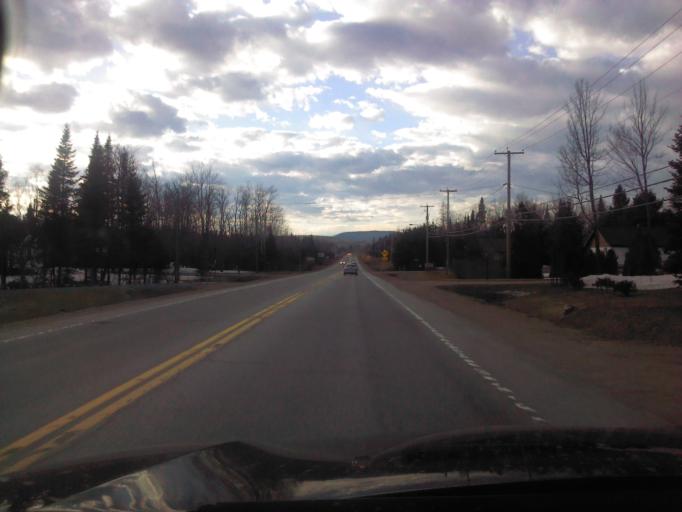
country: CA
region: Quebec
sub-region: Capitale-Nationale
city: Sainte Catherine de la Jacques Cartier
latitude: 46.8304
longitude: -71.5969
